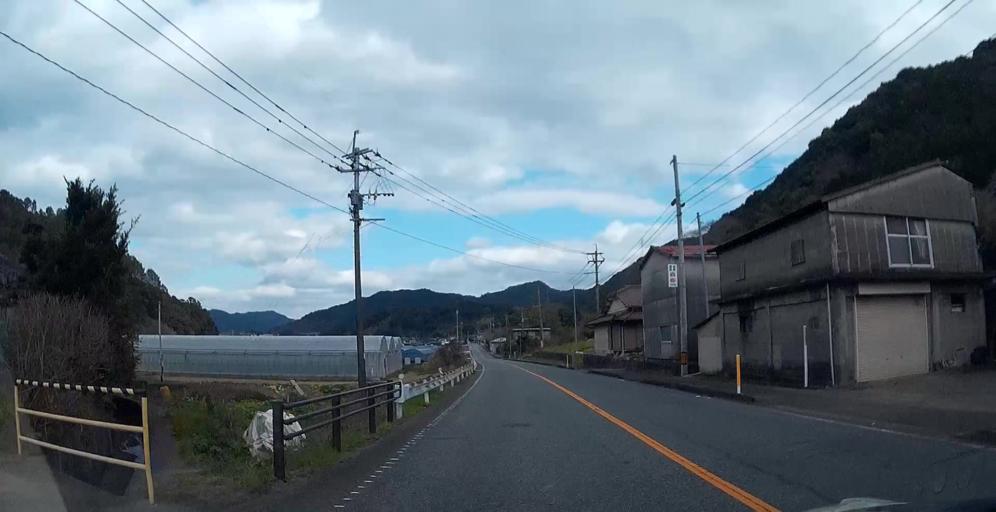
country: JP
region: Kumamoto
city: Minamata
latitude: 32.3417
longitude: 130.4979
